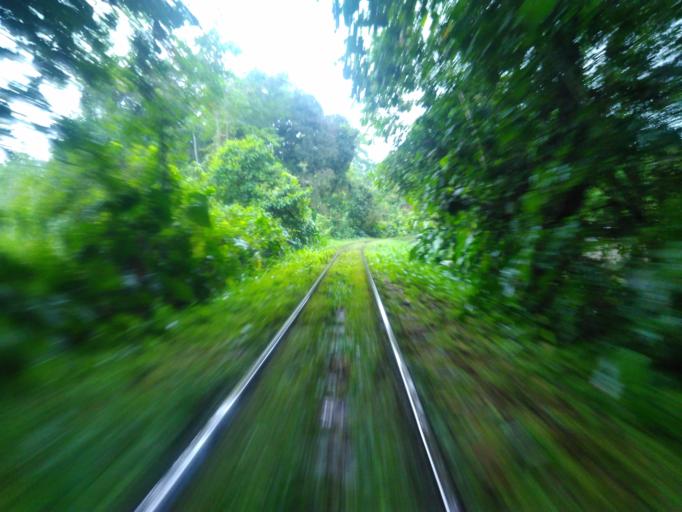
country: CO
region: Valle del Cauca
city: Buenaventura
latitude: 3.8439
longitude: -76.8788
